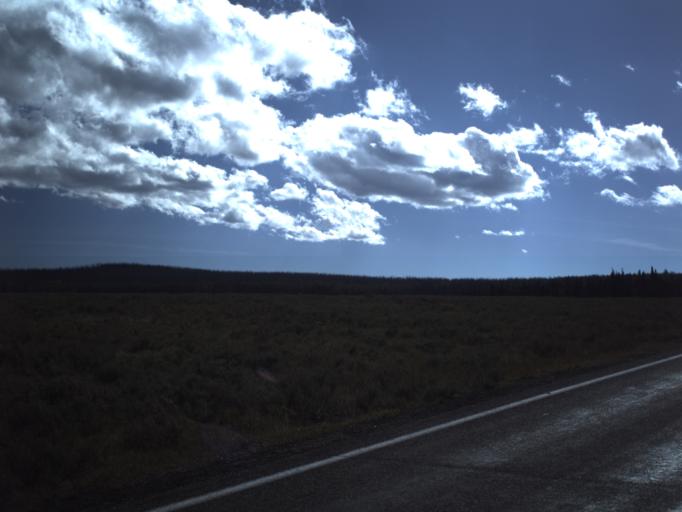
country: US
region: Utah
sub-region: Iron County
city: Parowan
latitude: 37.6508
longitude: -112.7867
